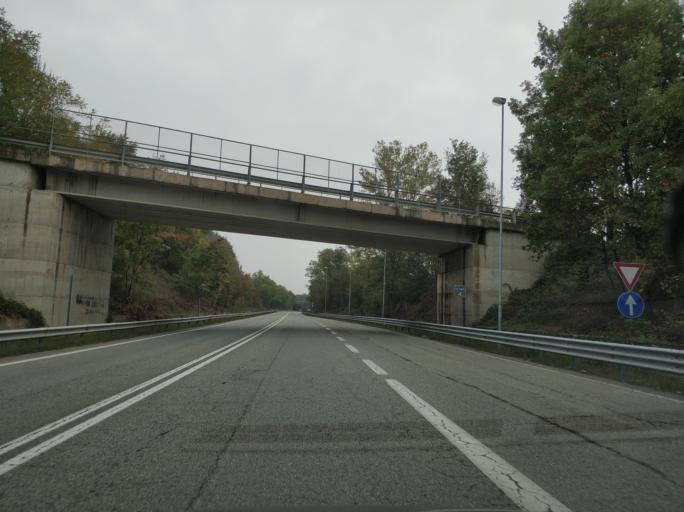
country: IT
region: Piedmont
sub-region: Provincia di Torino
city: Lombardore
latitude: 45.2143
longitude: 7.7328
